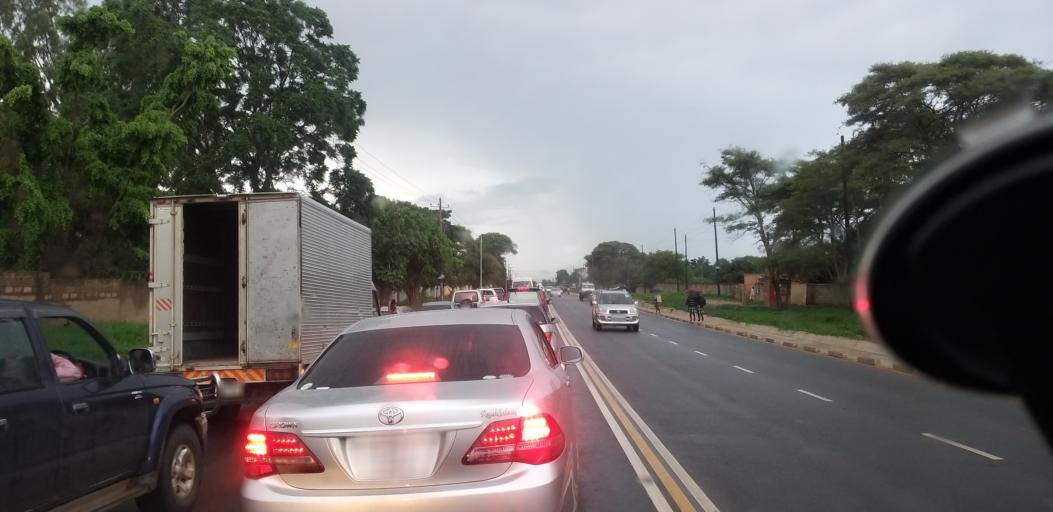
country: ZM
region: Lusaka
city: Lusaka
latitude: -15.4307
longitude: 28.3554
